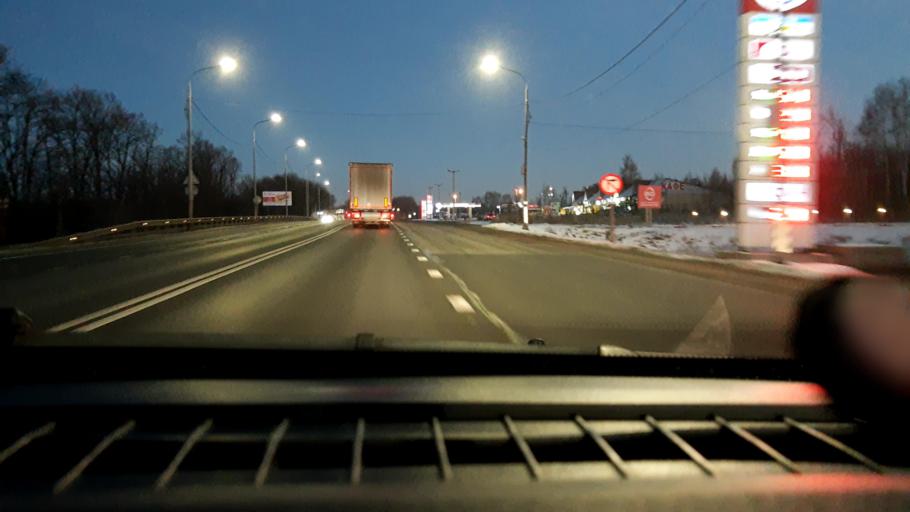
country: RU
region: Nizjnij Novgorod
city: Lyskovo
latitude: 56.0153
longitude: 45.0112
